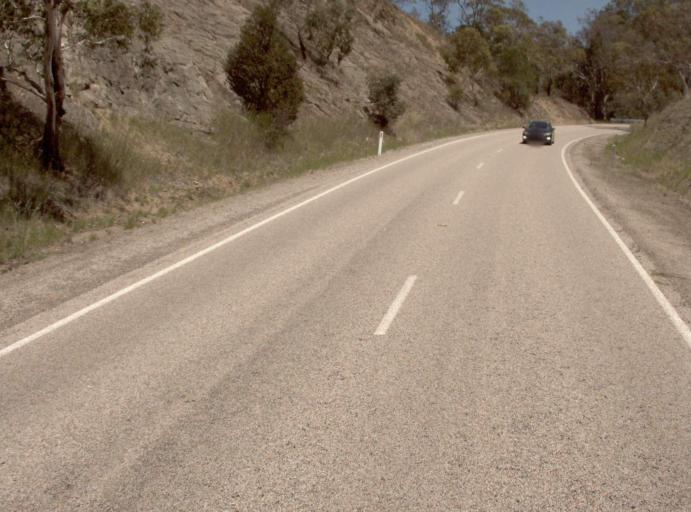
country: AU
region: Victoria
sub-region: Alpine
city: Mount Beauty
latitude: -37.1581
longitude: 147.6532
